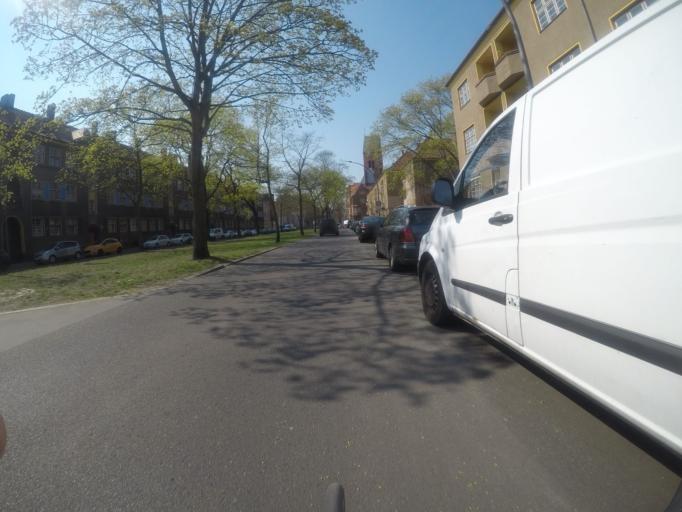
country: DE
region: Berlin
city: Wilhelmsruh
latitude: 52.5744
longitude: 13.3625
